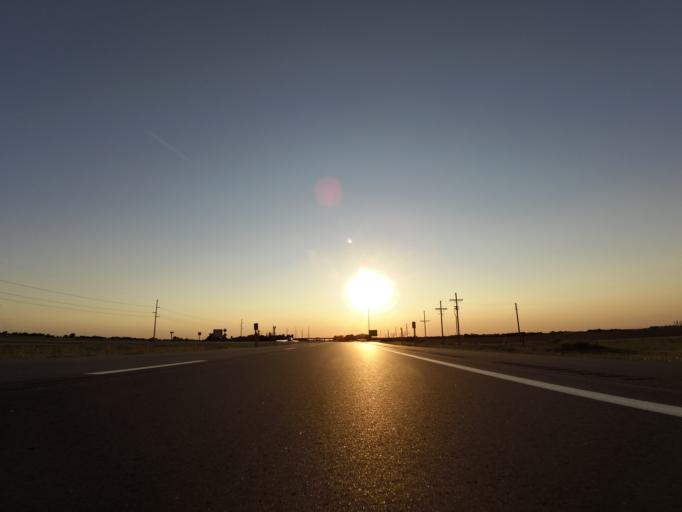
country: US
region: Kansas
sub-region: Reno County
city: South Hutchinson
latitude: 38.0135
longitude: -97.9575
